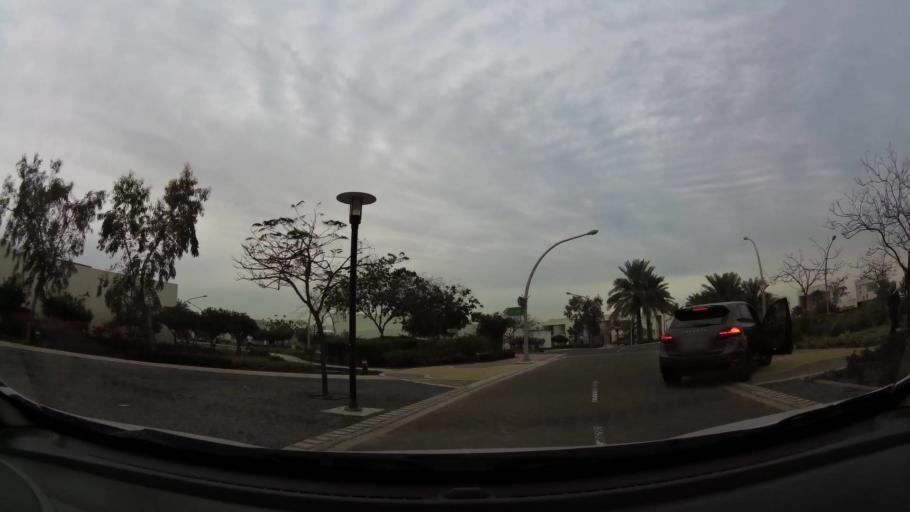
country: BH
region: Central Governorate
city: Dar Kulayb
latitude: 25.8327
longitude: 50.6157
